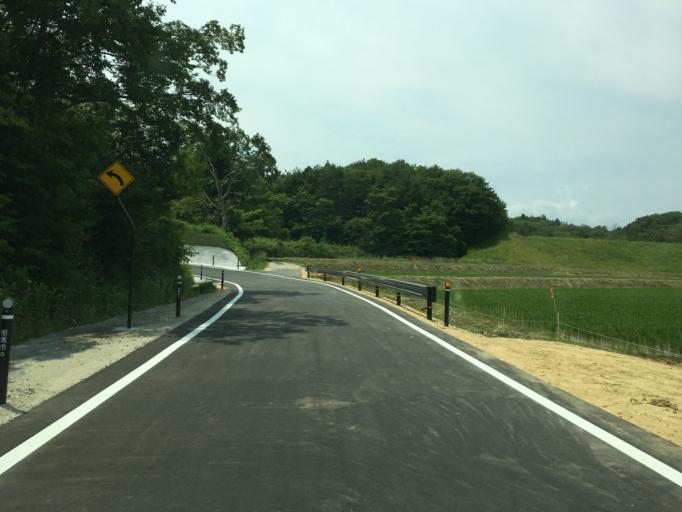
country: JP
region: Miyagi
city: Marumori
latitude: 37.7575
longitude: 140.9740
